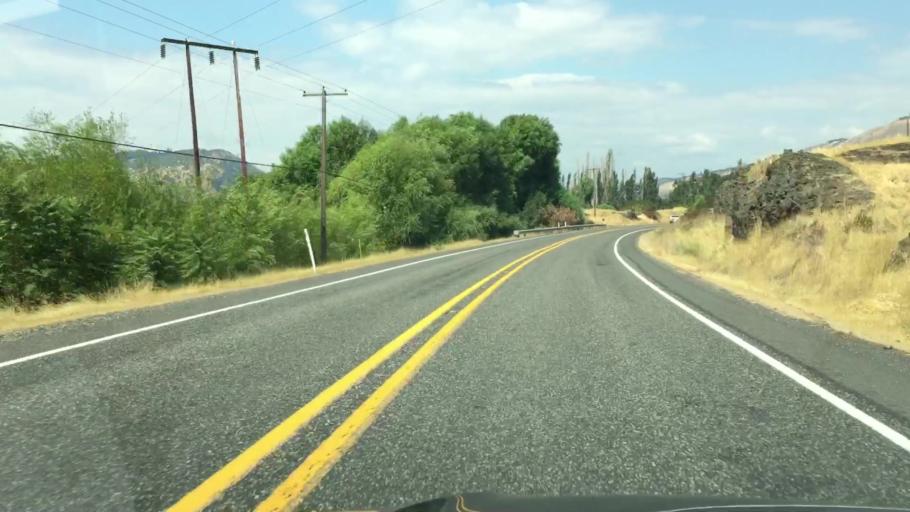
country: US
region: Washington
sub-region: Klickitat County
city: Dallesport
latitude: 45.6496
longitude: -121.1834
